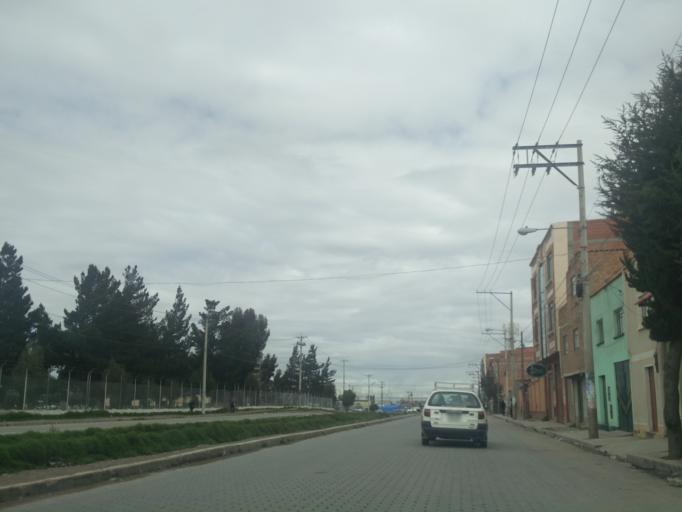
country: BO
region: La Paz
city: La Paz
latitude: -16.5242
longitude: -68.1672
